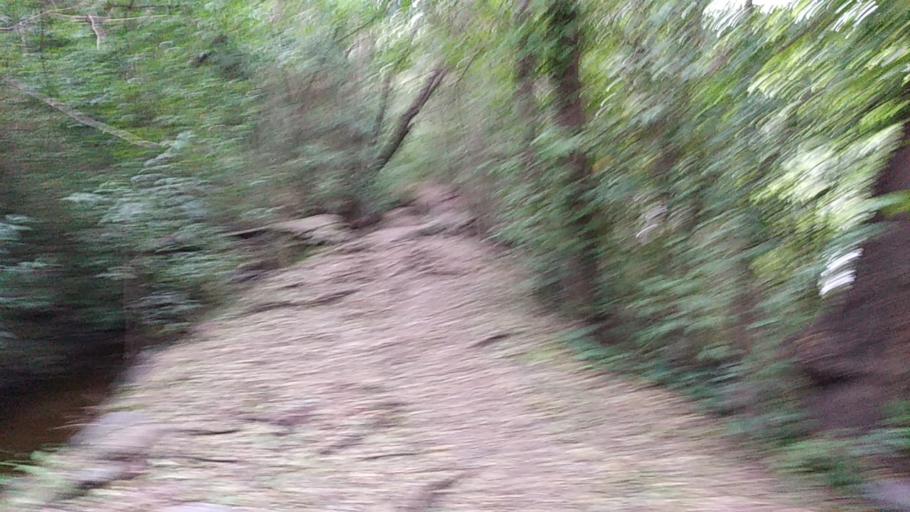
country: AR
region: Cordoba
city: Alta Gracia
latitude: -31.7251
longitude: -64.4355
